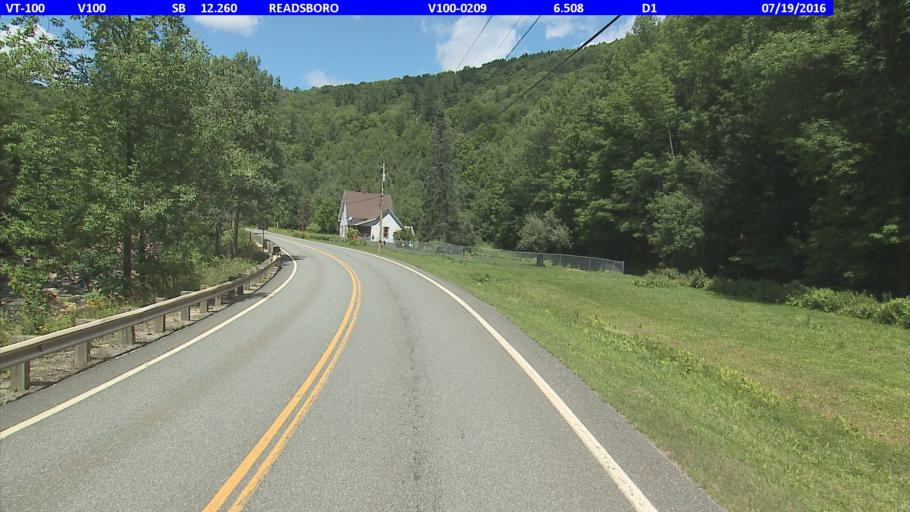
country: US
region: Massachusetts
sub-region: Franklin County
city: Charlemont
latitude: 42.7771
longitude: -72.9516
